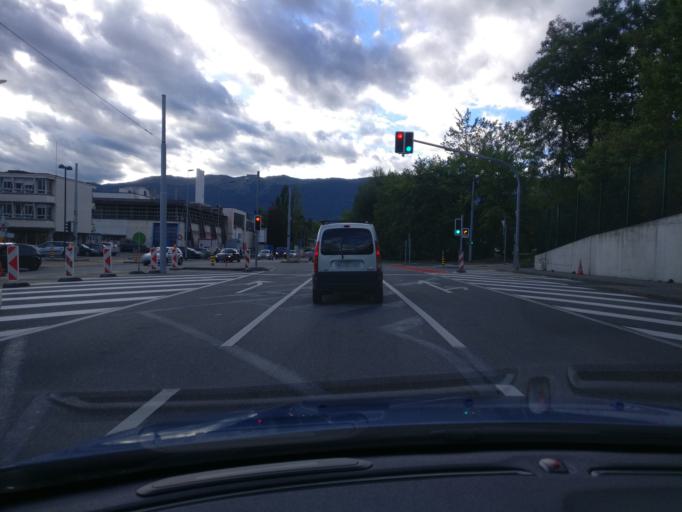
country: CH
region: Geneva
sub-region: Geneva
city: Satigny
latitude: 46.2341
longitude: 6.0537
